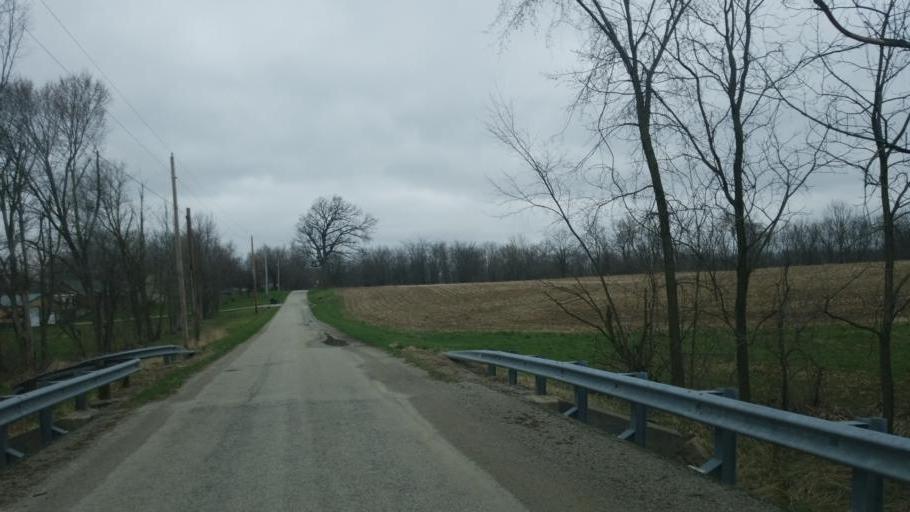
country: US
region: Ohio
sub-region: Hardin County
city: Forest
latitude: 40.6747
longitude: -83.3907
